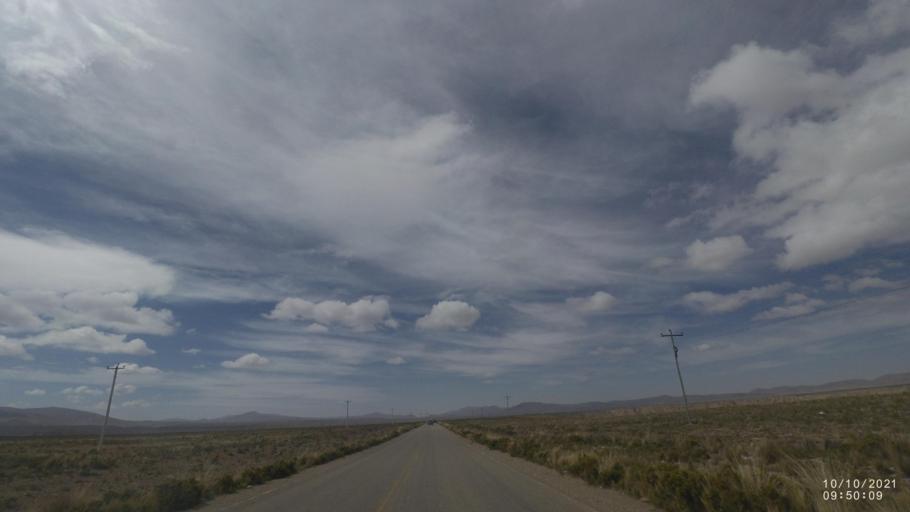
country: BO
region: La Paz
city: Colquiri
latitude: -17.2383
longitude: -67.3345
